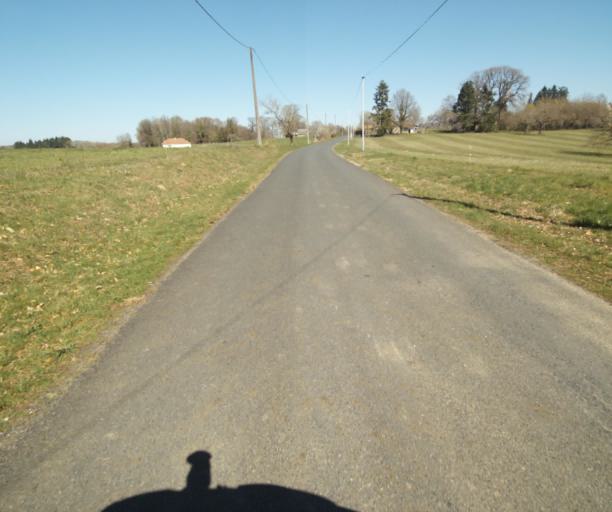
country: FR
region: Limousin
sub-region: Departement de la Correze
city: Saint-Mexant
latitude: 45.3192
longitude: 1.6464
